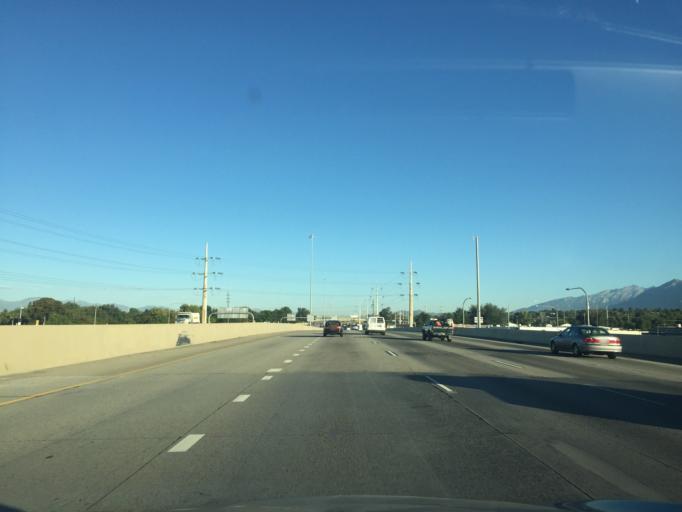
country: US
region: Utah
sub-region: Utah County
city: Provo
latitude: 40.2336
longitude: -111.6845
